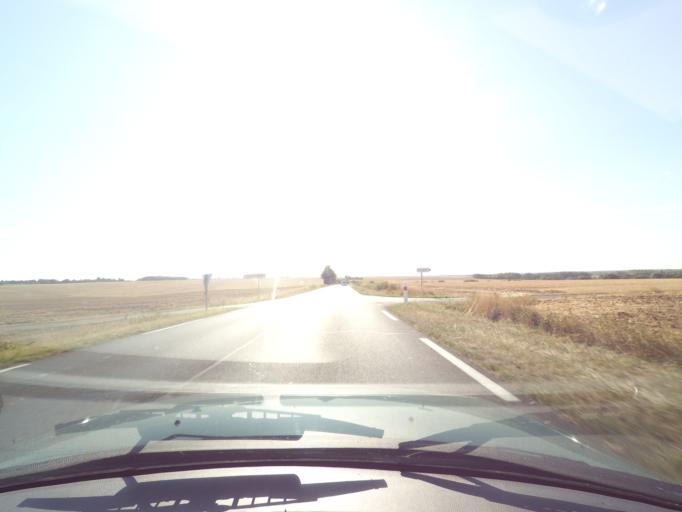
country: FR
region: Poitou-Charentes
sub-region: Departement de la Vienne
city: Ayron
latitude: 46.6550
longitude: 0.1094
